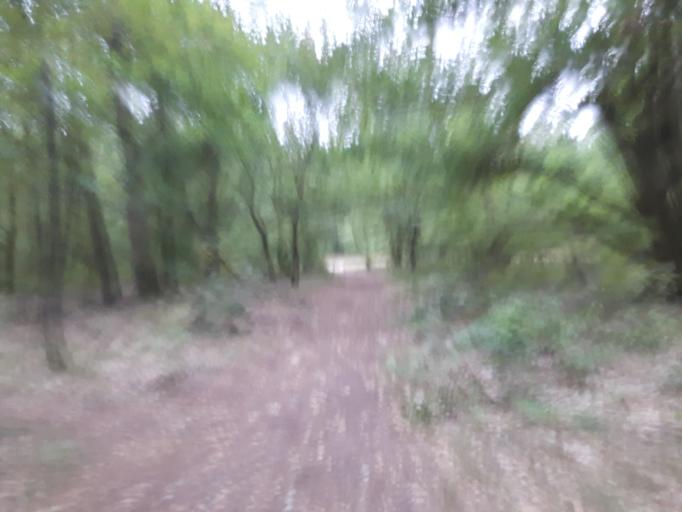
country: DE
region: Lower Saxony
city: Delmenhorst
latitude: 53.0168
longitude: 8.6852
